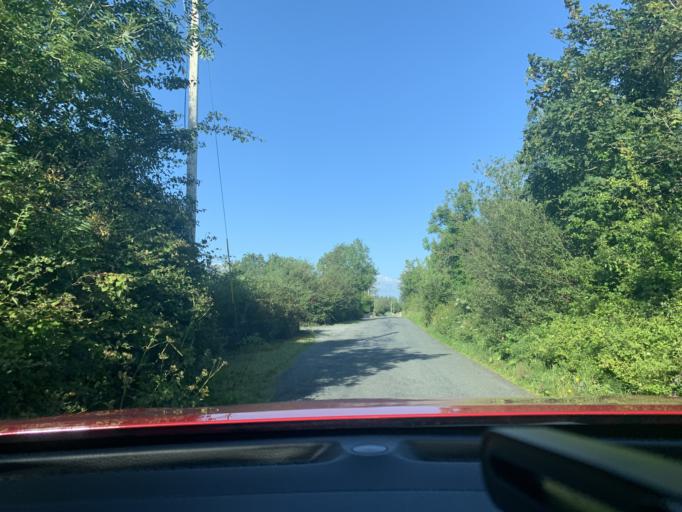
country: IE
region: Connaught
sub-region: Sligo
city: Tobercurry
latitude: 54.1201
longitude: -8.7527
